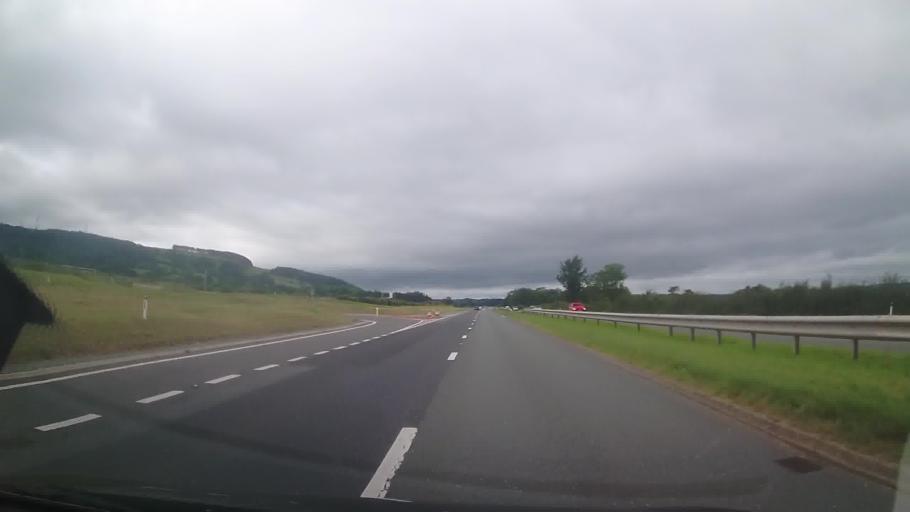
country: GB
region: Wales
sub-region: Gwynedd
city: Aber
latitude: 53.2305
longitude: -4.0332
